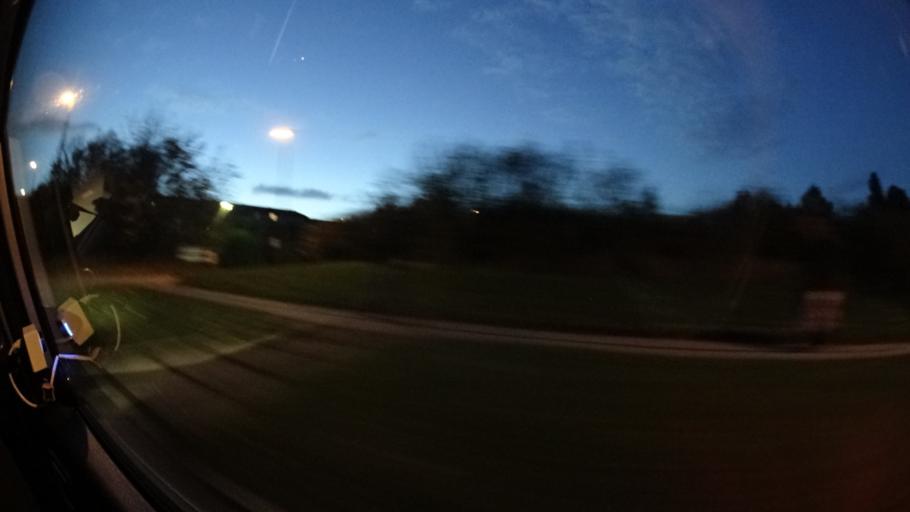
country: DK
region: South Denmark
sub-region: Odense Kommune
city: Neder Holluf
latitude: 55.3626
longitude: 10.4579
